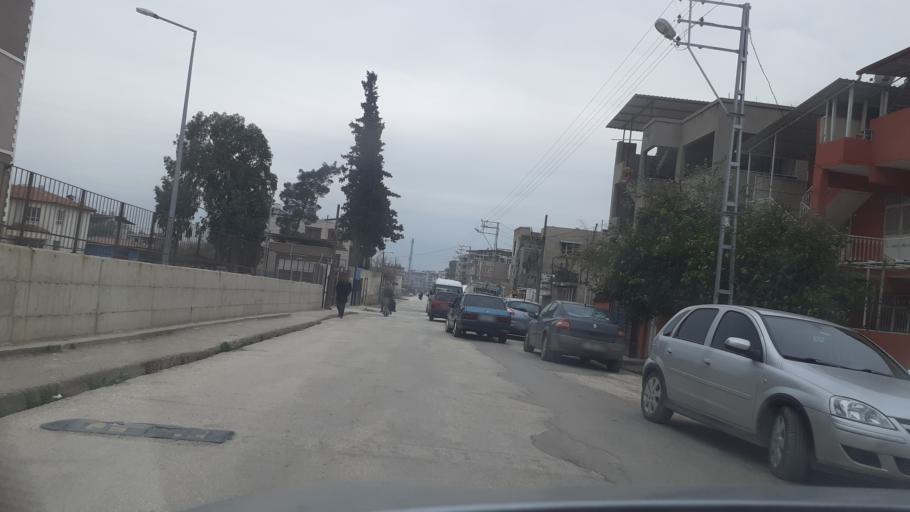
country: TR
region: Hatay
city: Kirikhan
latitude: 36.4877
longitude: 36.3557
